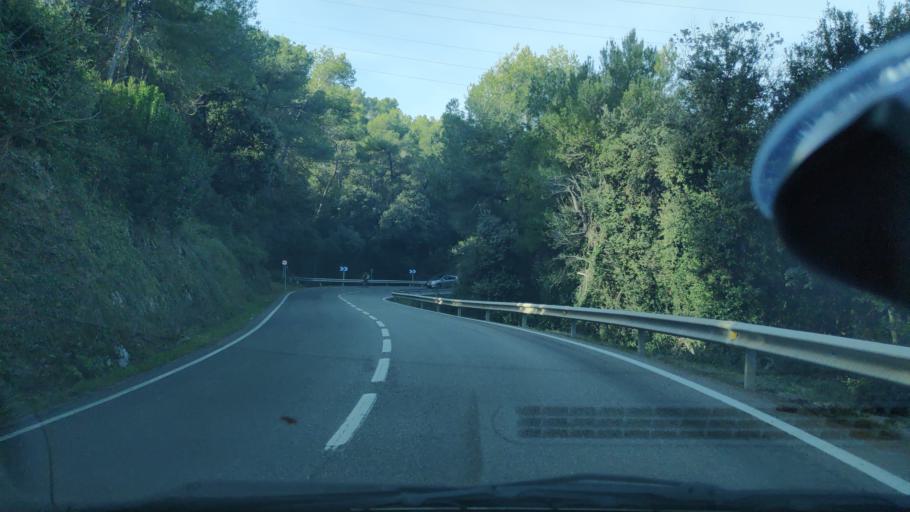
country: ES
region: Catalonia
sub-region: Provincia de Barcelona
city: Castellar del Valles
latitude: 41.6050
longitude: 2.0648
